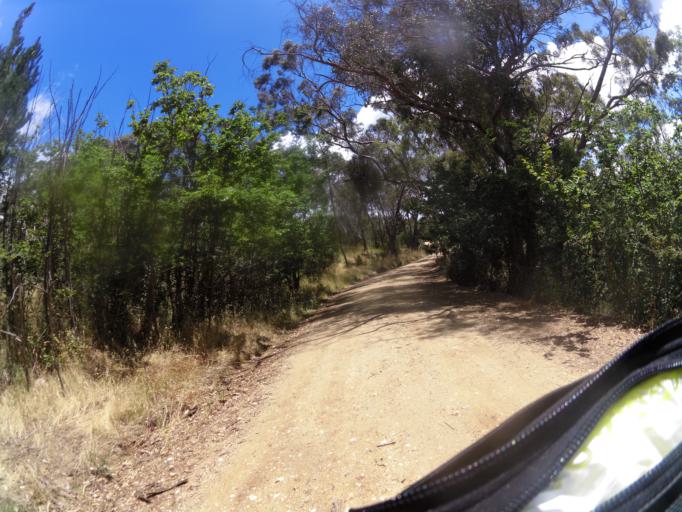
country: AU
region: Victoria
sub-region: Mount Alexander
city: Castlemaine
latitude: -37.0565
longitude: 144.2716
